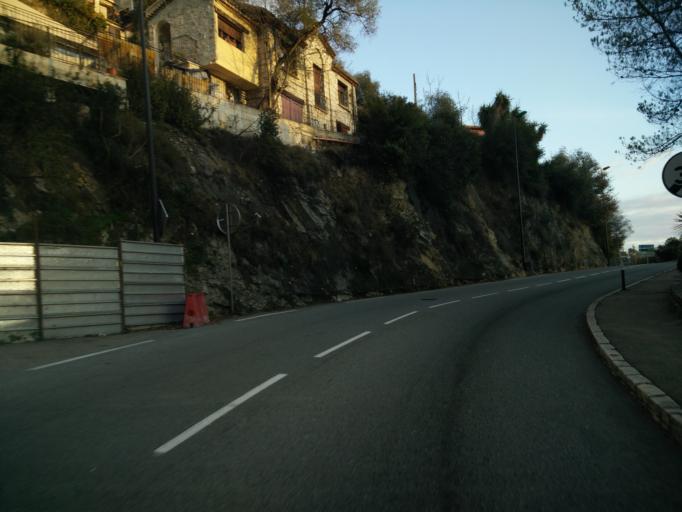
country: FR
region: Provence-Alpes-Cote d'Azur
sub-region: Departement des Alpes-Maritimes
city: Eze
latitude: 43.7312
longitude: 7.3647
